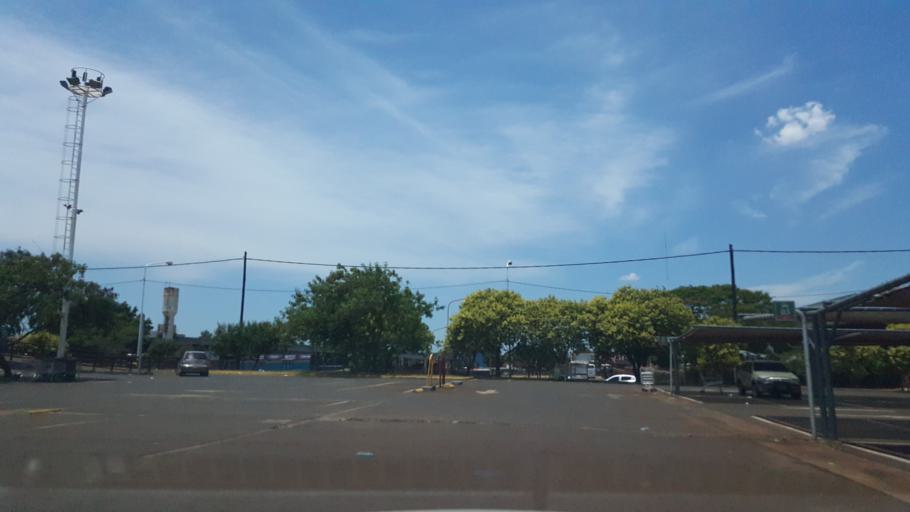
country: AR
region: Misiones
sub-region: Departamento de Capital
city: Posadas
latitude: -27.4021
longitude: -55.9166
